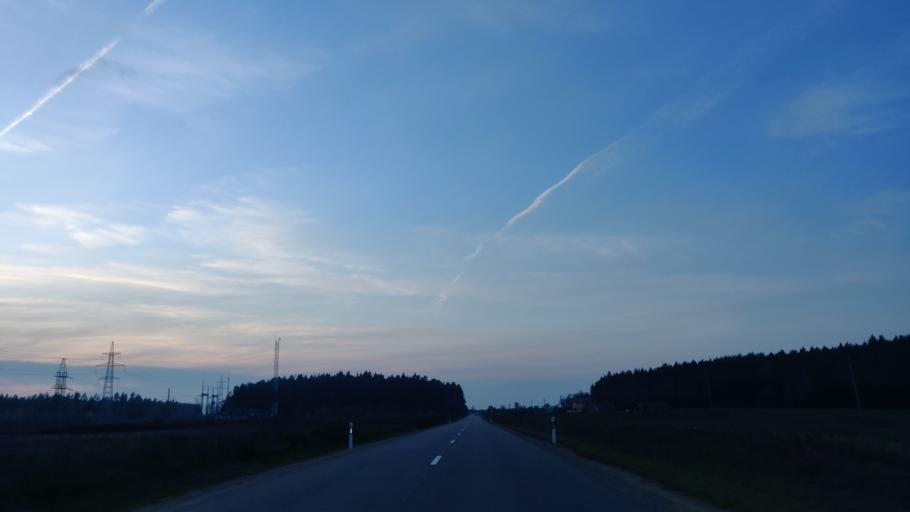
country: LT
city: Lentvaris
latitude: 54.5967
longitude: 25.0321
